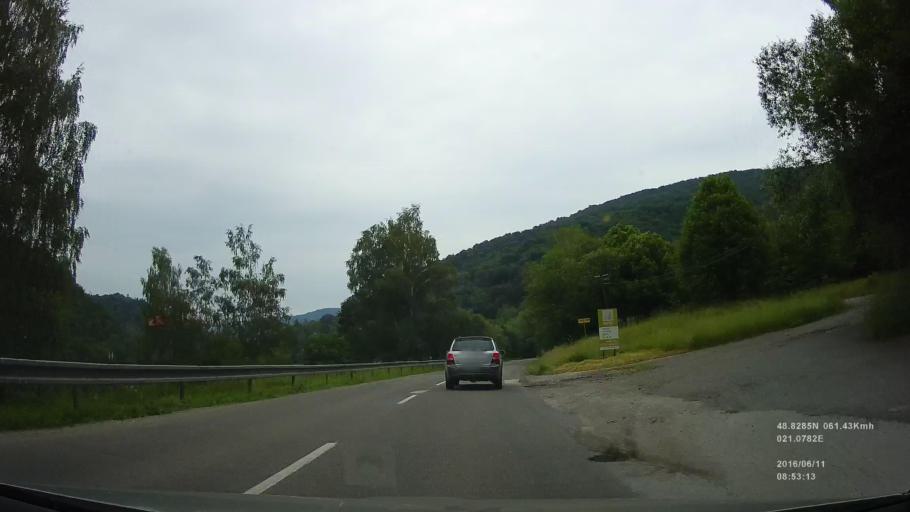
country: SK
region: Kosicky
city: Gelnica
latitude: 48.8237
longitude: 21.0808
